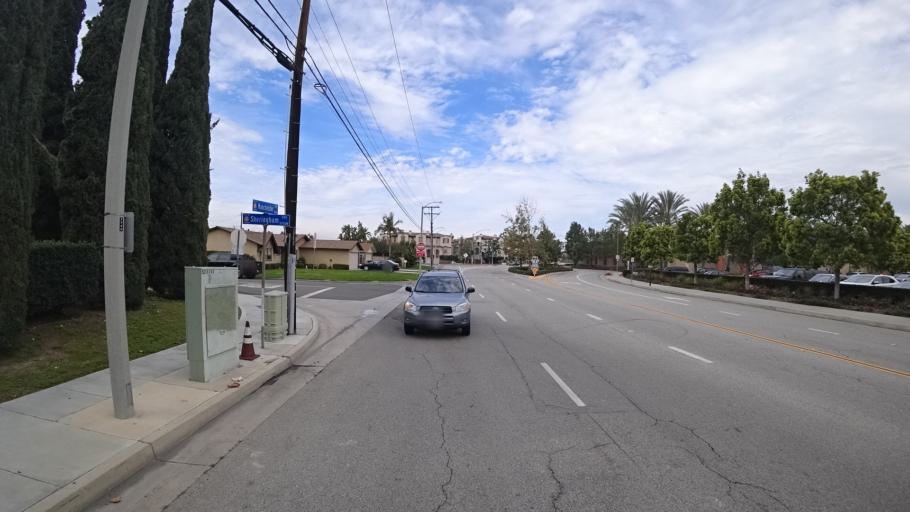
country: US
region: California
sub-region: Orange County
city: Orange
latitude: 33.7898
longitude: -117.8932
